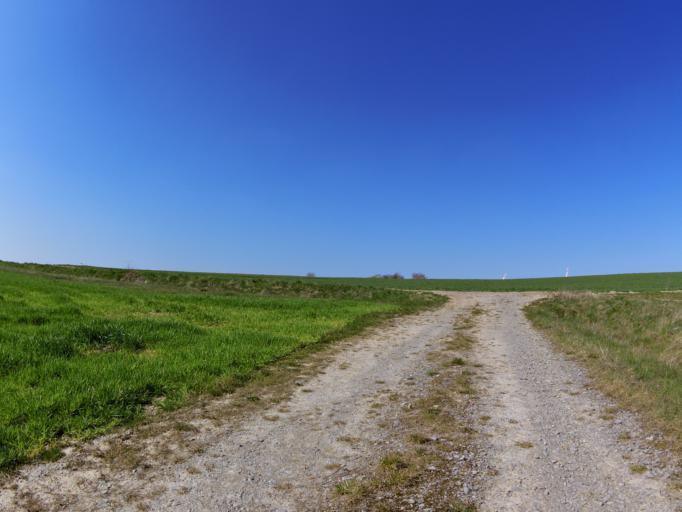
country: DE
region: Bavaria
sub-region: Regierungsbezirk Unterfranken
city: Biebelried
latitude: 49.7366
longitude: 10.1018
